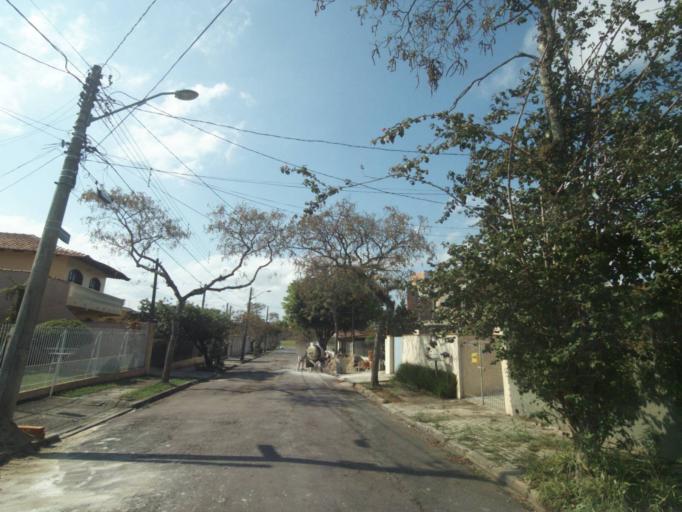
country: BR
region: Parana
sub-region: Pinhais
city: Pinhais
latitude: -25.4050
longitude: -49.2135
